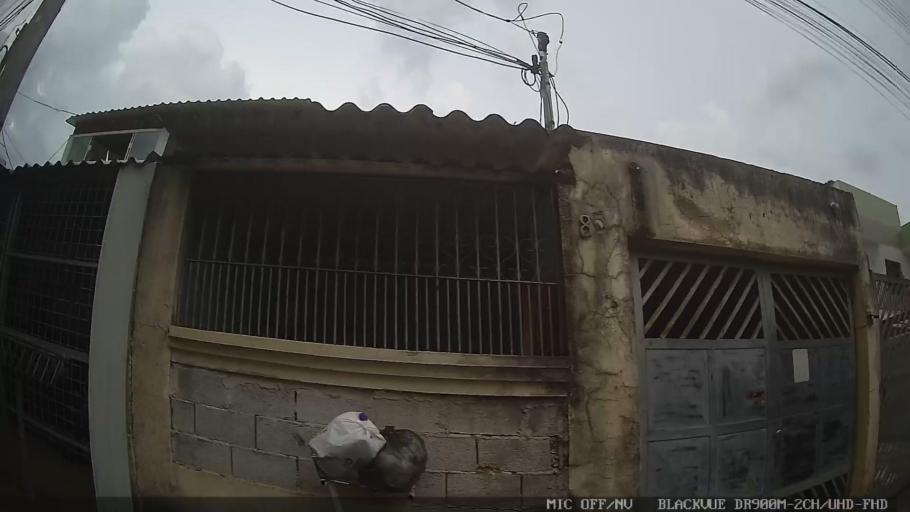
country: BR
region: Sao Paulo
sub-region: Atibaia
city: Atibaia
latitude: -23.1281
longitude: -46.5565
